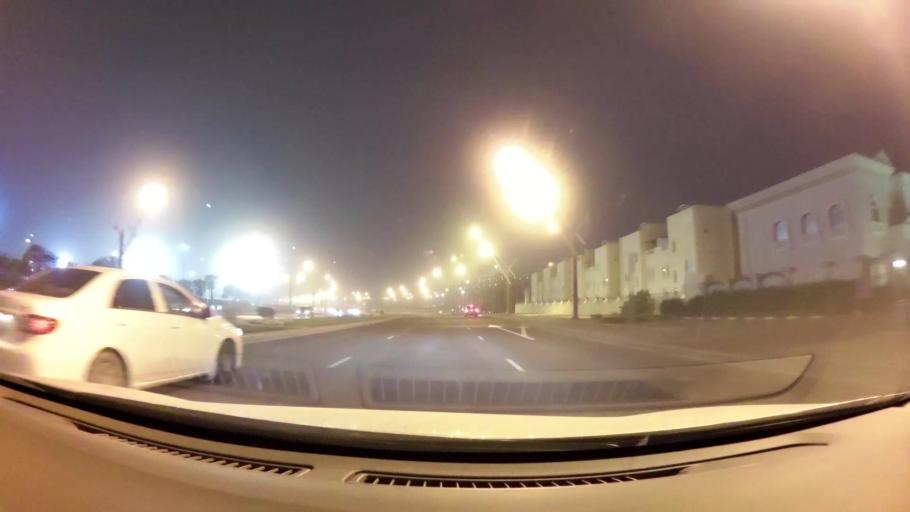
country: QA
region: Baladiyat ar Rayyan
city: Ar Rayyan
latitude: 25.2645
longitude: 51.4528
